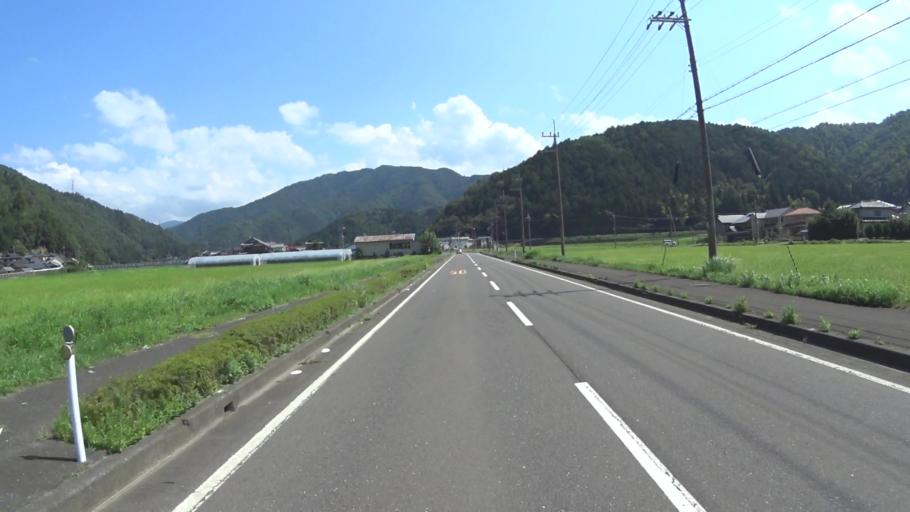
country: JP
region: Fukui
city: Obama
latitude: 35.4129
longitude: 135.6812
